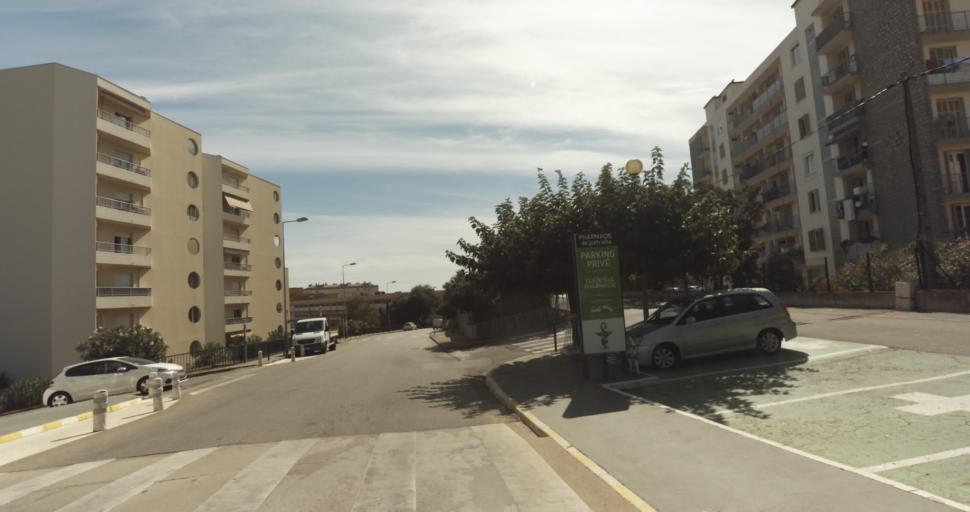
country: FR
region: Corsica
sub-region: Departement de la Corse-du-Sud
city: Ajaccio
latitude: 41.9359
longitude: 8.7562
